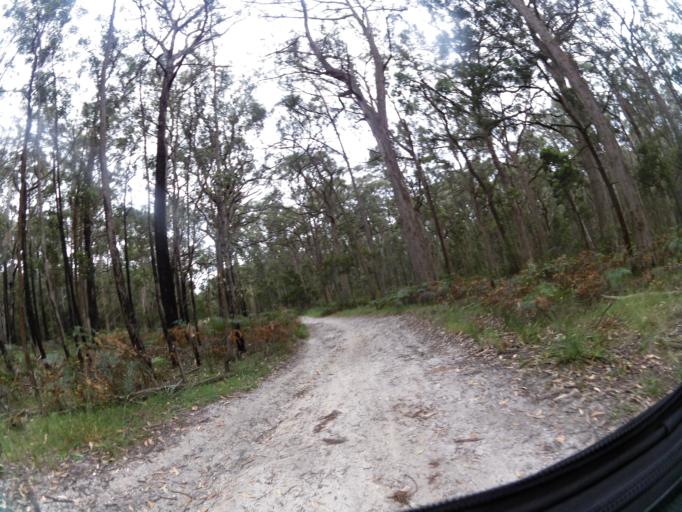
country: AU
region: Victoria
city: Brown Hill
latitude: -37.5090
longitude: 143.9112
